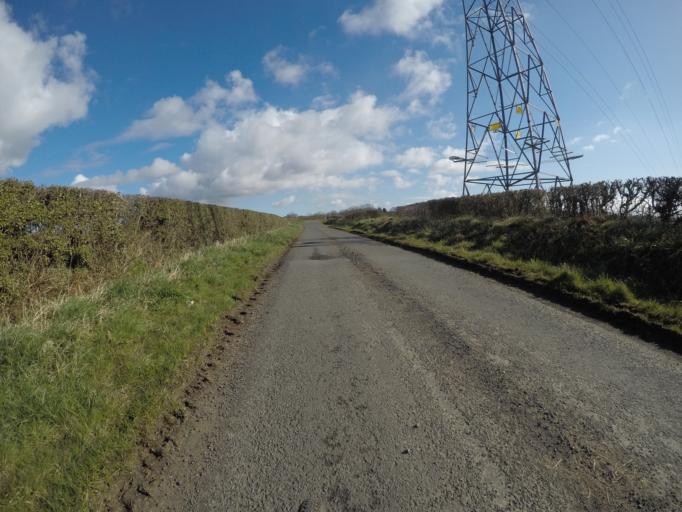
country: GB
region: Scotland
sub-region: North Ayrshire
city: Irvine
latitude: 55.6598
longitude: -4.6530
